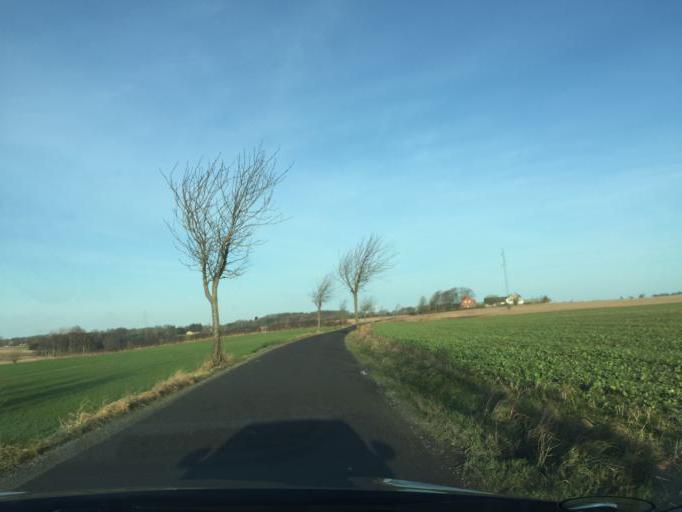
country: DK
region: South Denmark
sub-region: Middelfart Kommune
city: Ejby
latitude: 55.4522
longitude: 9.9289
